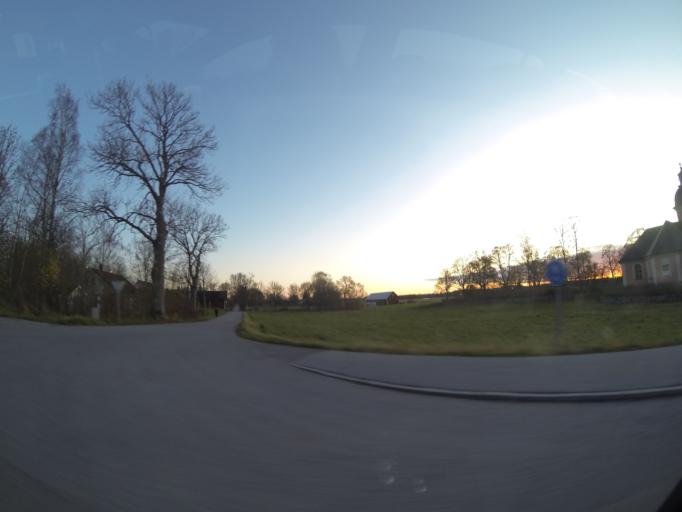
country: SE
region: OErebro
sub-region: Orebro Kommun
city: Hovsta
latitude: 59.3147
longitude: 15.3391
